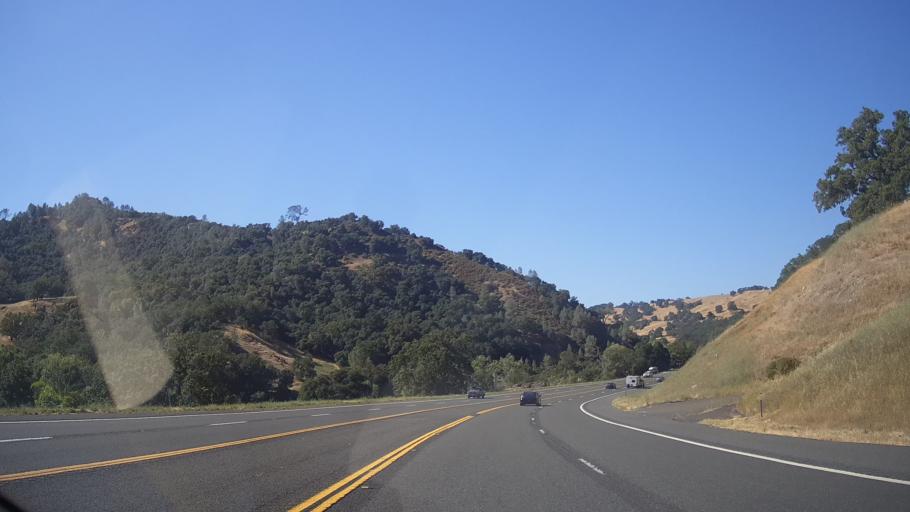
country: US
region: California
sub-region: Sonoma County
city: Cloverdale
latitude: 38.9178
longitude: -123.0584
